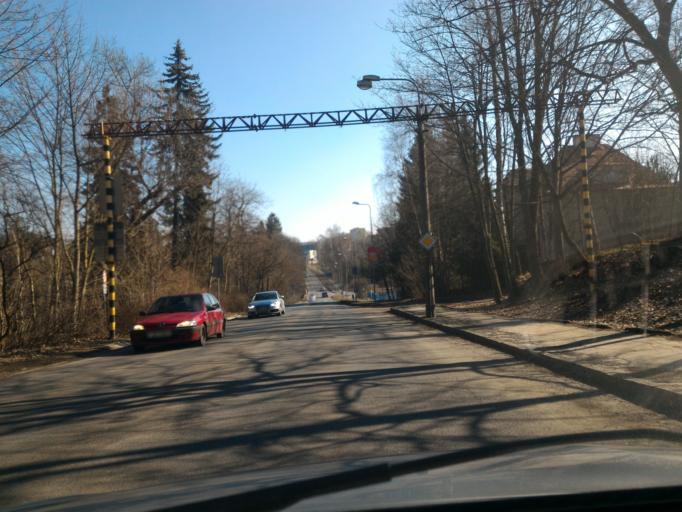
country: CZ
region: Liberecky
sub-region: Okres Jablonec nad Nisou
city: Jablonec nad Nisou
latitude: 50.7317
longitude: 15.1717
